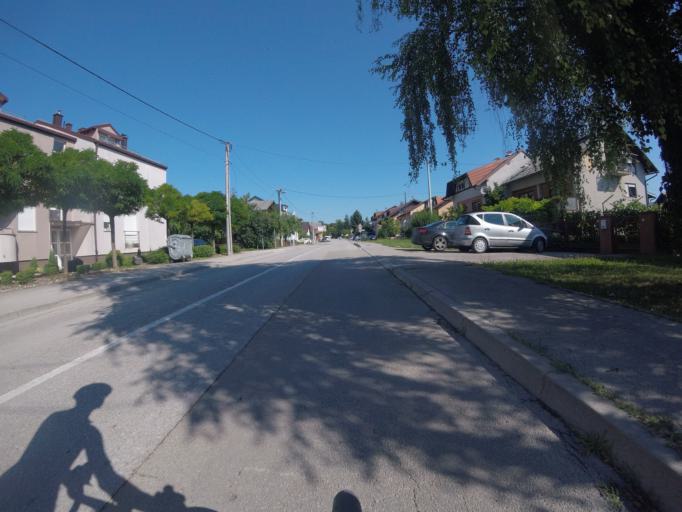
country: HR
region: Zagrebacka
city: Bregana
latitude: 45.8265
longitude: 15.6955
